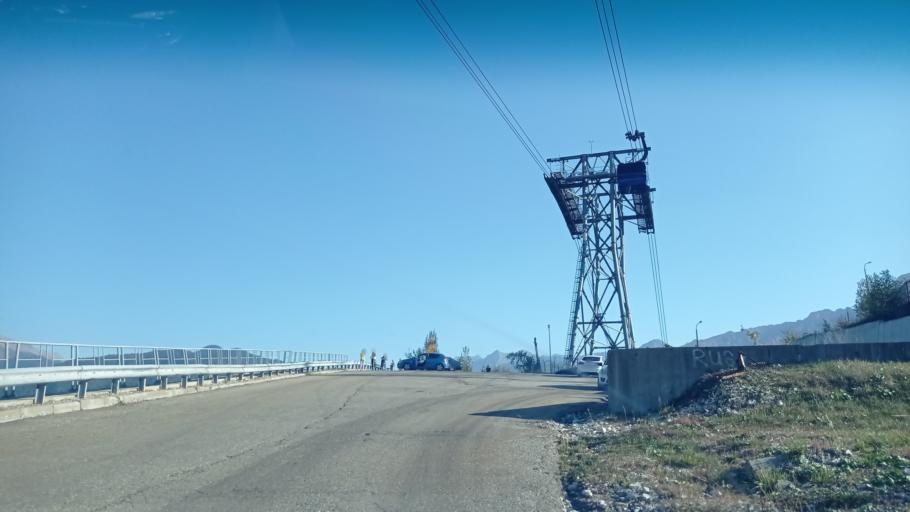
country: RU
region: Krasnodarskiy
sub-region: Sochi City
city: Krasnaya Polyana
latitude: 43.6609
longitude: 40.3236
